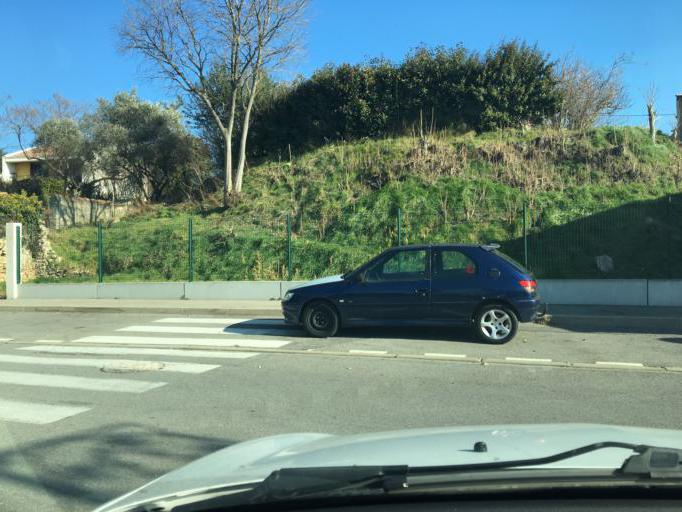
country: FR
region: Provence-Alpes-Cote d'Azur
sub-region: Departement des Bouches-du-Rhone
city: Mallemort
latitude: 43.7269
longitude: 5.1812
